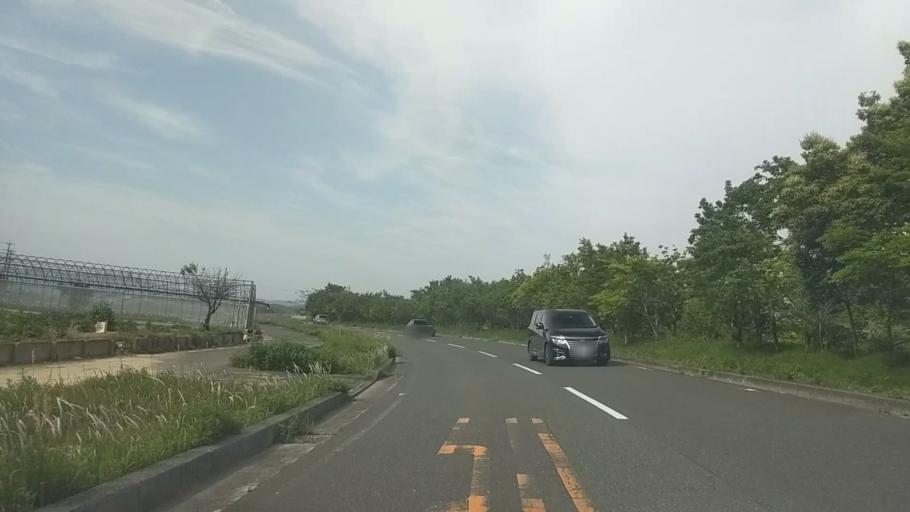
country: JP
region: Shizuoka
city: Kosai-shi
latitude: 34.7284
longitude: 137.6059
